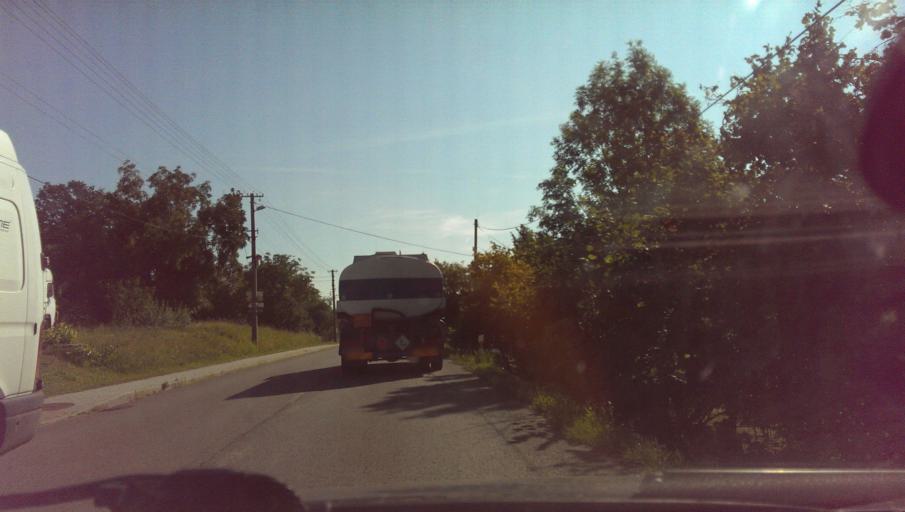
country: CZ
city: Staric
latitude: 49.6902
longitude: 18.2920
